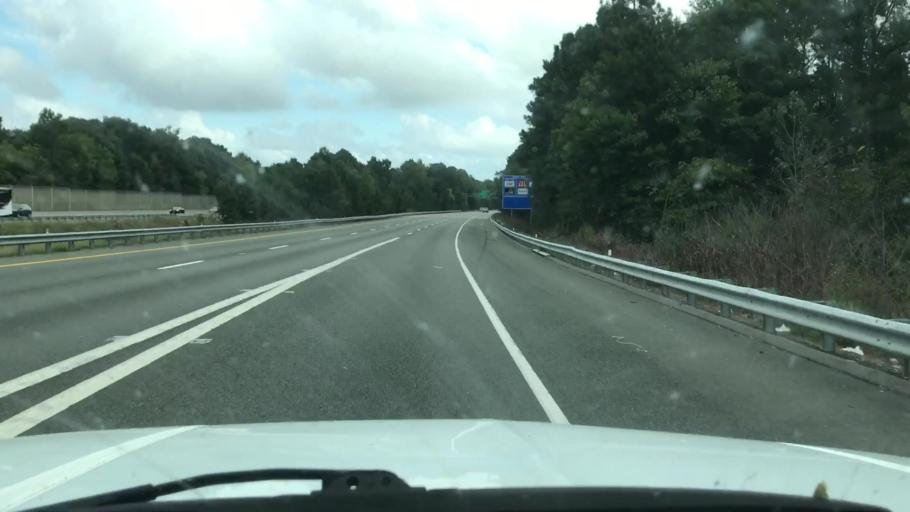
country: US
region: Virginia
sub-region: Henrico County
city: Short Pump
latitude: 37.6623
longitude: -77.5979
